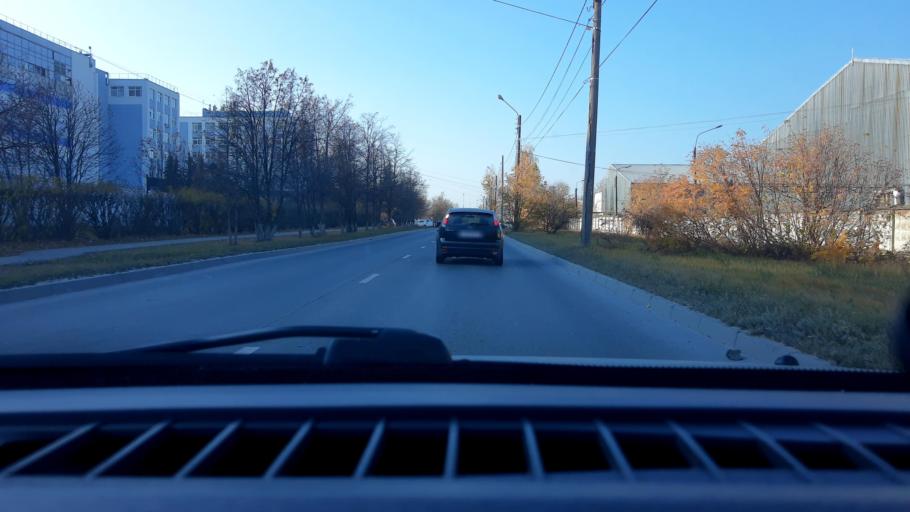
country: RU
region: Nizjnij Novgorod
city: Gorbatovka
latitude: 56.3500
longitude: 43.8085
